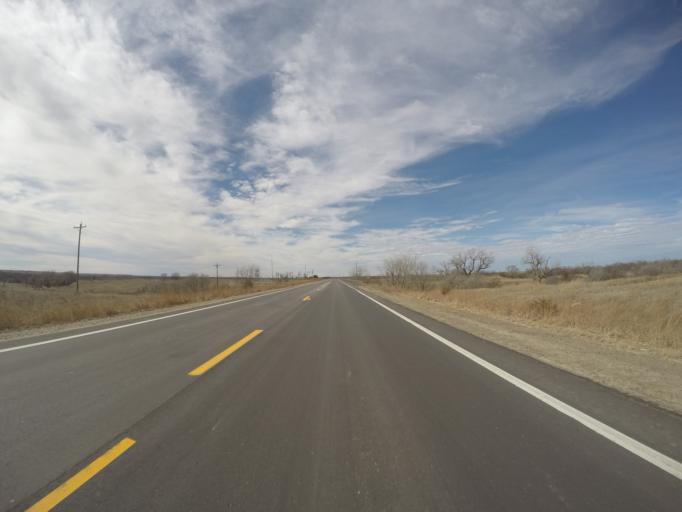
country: US
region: Nebraska
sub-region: Franklin County
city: Franklin
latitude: 40.0970
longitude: -98.8166
